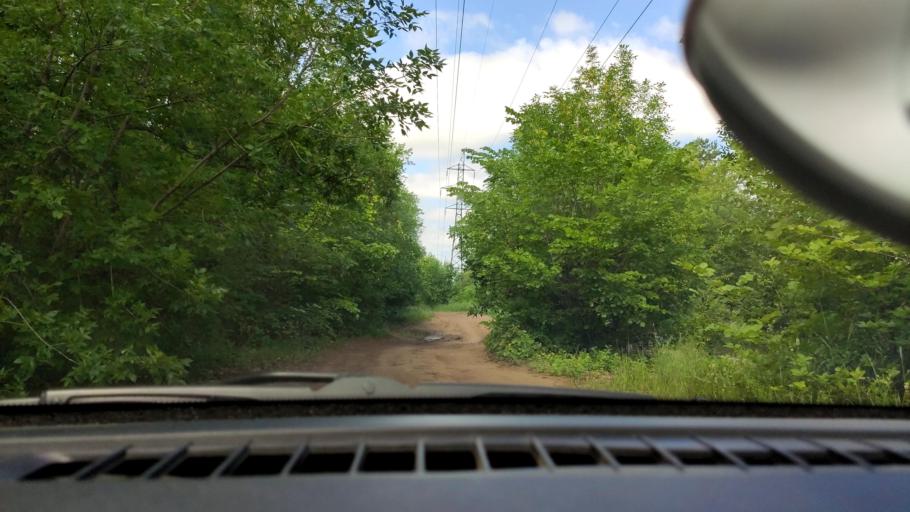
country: RU
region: Samara
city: Samara
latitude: 53.1263
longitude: 50.1856
